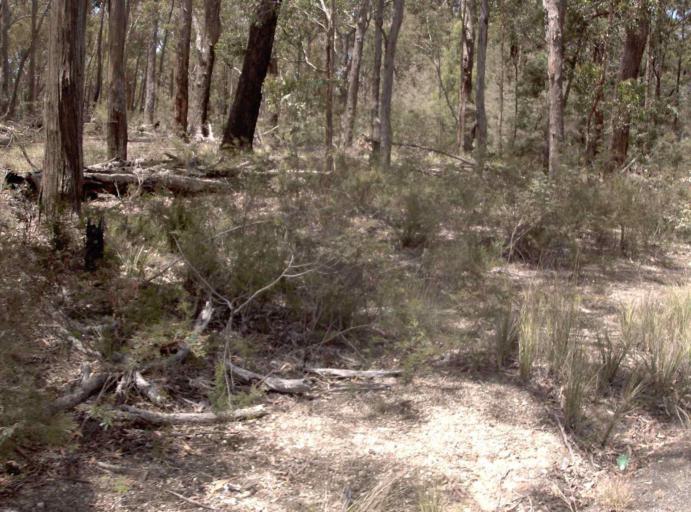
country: AU
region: Victoria
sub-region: East Gippsland
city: Lakes Entrance
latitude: -37.5927
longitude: 147.8930
